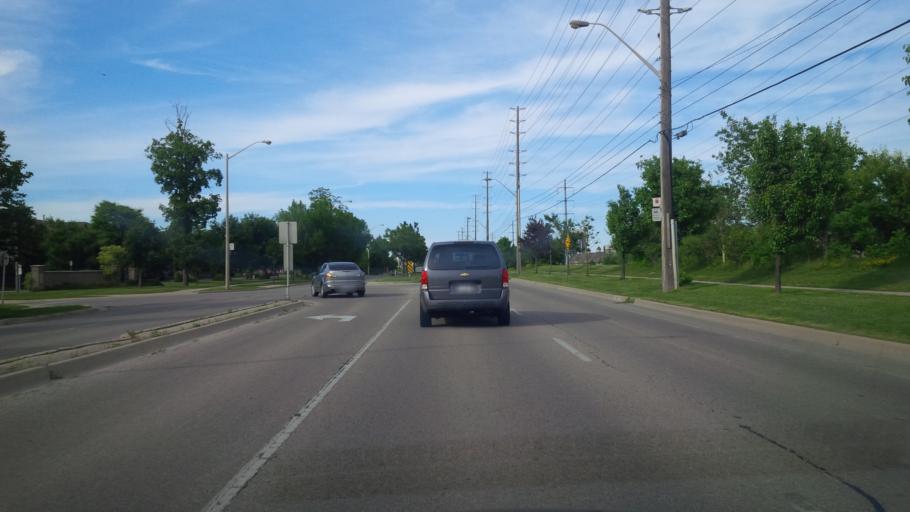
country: CA
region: Ontario
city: Burlington
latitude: 43.3861
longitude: -79.7986
